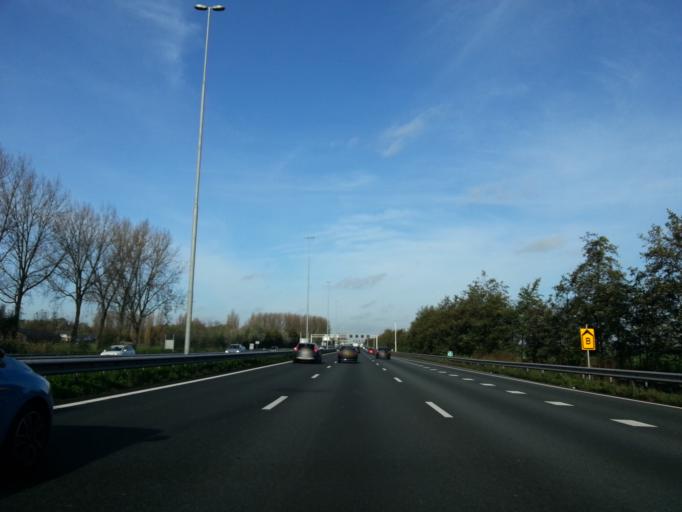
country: NL
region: South Holland
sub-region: Gemeente Schiedam
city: Schiedam
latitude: 51.9542
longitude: 4.4132
